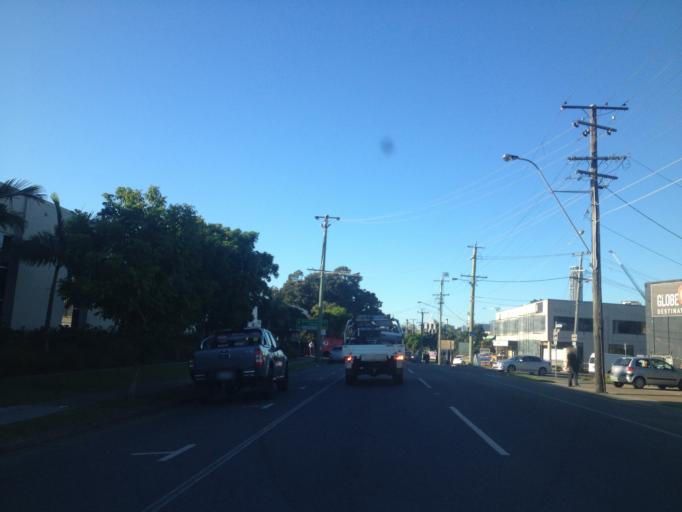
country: AU
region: Queensland
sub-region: Brisbane
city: Milton
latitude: -27.4806
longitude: 153.0049
